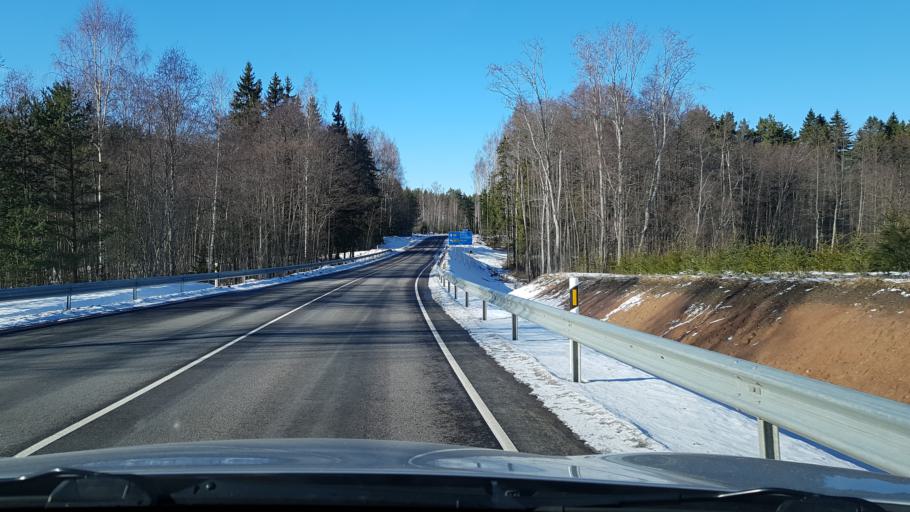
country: RU
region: Pskov
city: Pechory
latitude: 57.9754
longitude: 27.5767
